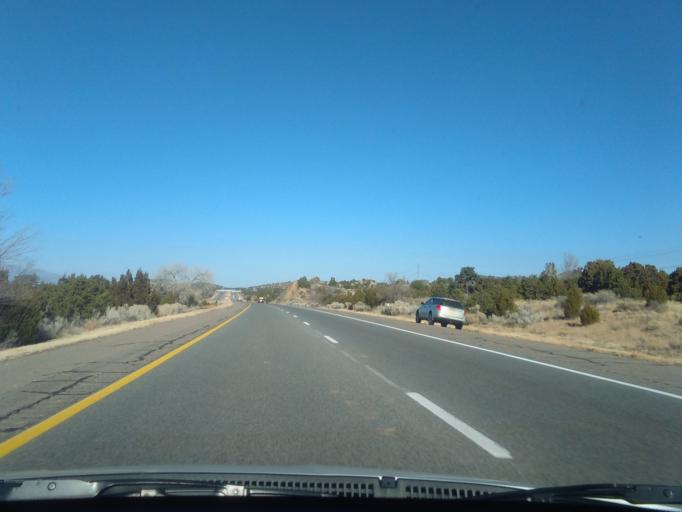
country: US
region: New Mexico
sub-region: Santa Fe County
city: Eldorado at Santa Fe
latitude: 35.5884
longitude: -105.9020
